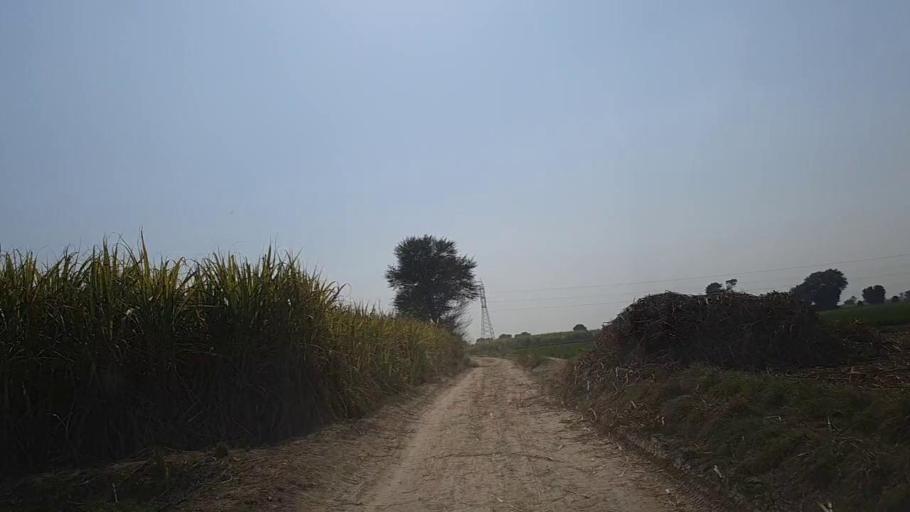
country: PK
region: Sindh
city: Moro
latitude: 26.6931
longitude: 67.9276
